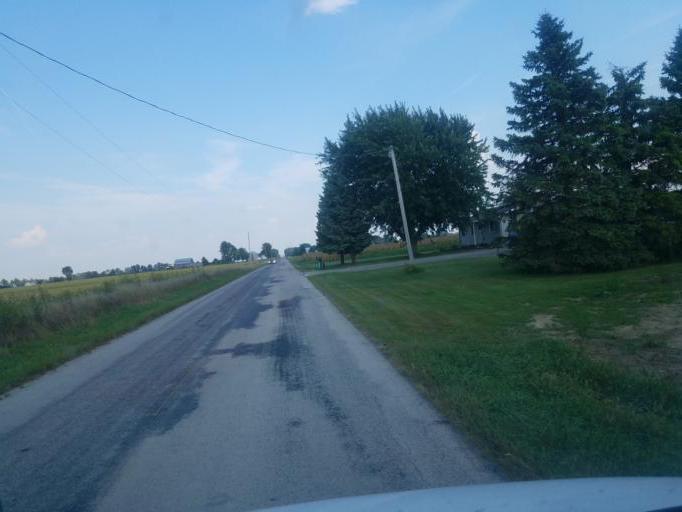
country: US
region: Ohio
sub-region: Wyandot County
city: Carey
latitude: 40.9049
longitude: -83.4760
